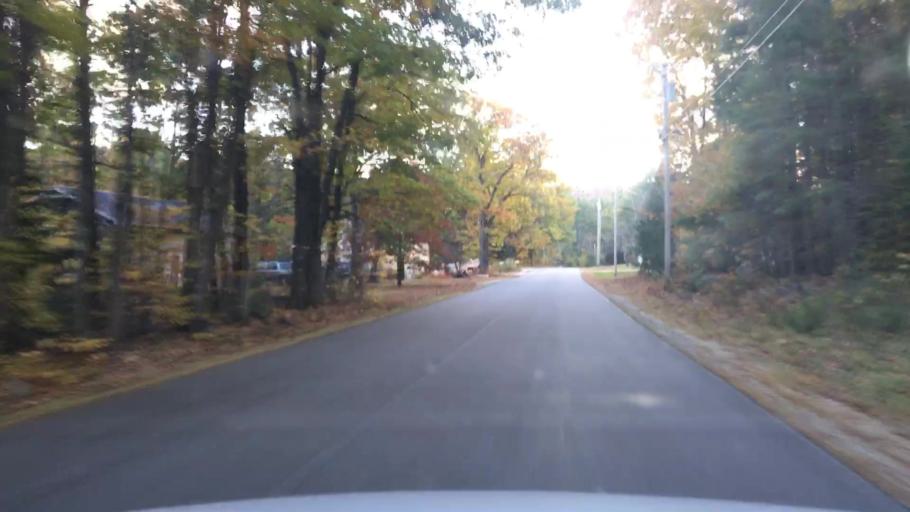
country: US
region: Maine
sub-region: Cumberland County
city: Harrison
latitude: 44.2377
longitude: -70.7456
